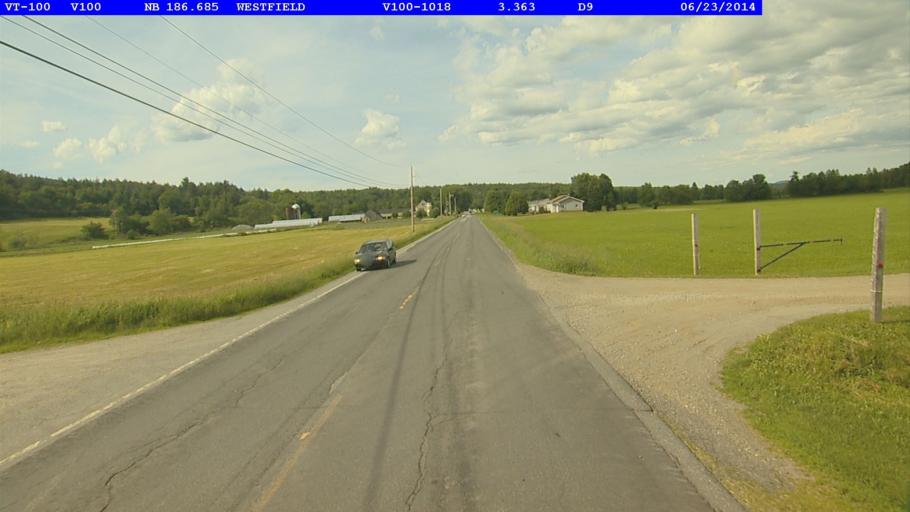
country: US
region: Vermont
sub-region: Orleans County
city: Newport
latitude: 44.8831
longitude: -72.4297
